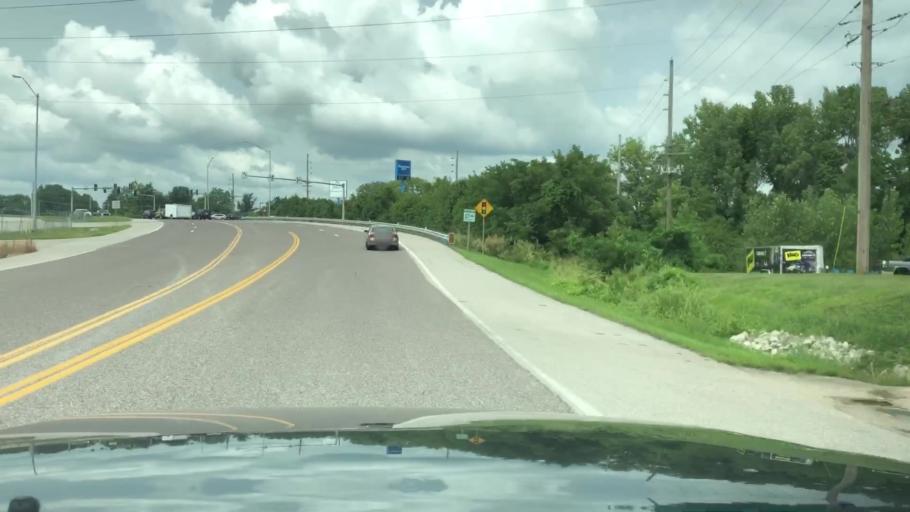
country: US
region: Missouri
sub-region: Saint Charles County
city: Saint Peters
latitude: 38.7939
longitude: -90.5626
